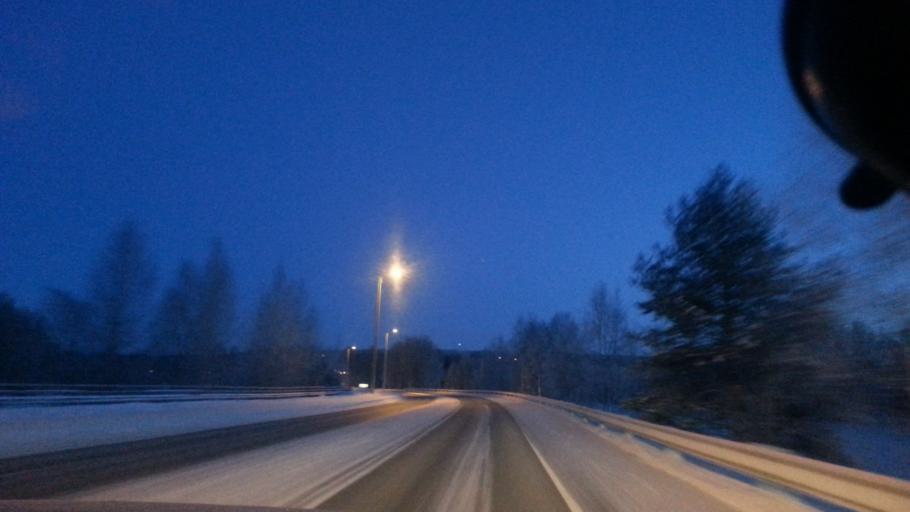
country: FI
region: Lapland
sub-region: Rovaniemi
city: Rovaniemi
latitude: 66.4839
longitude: 25.7481
